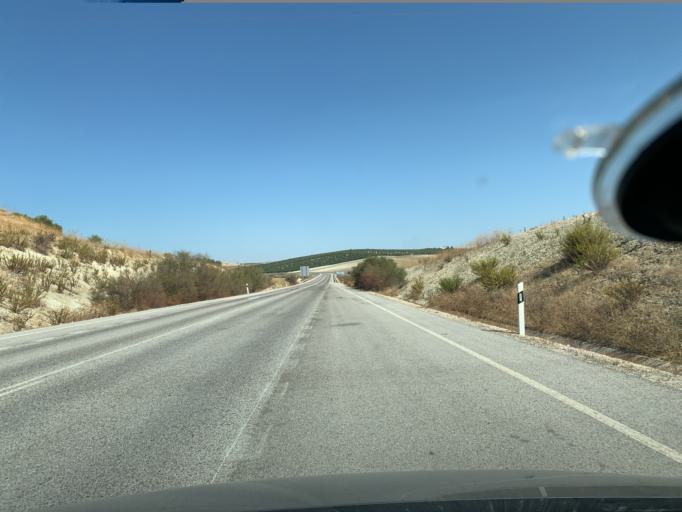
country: ES
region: Andalusia
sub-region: Provincia de Sevilla
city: Marchena
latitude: 37.3158
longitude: -5.3975
